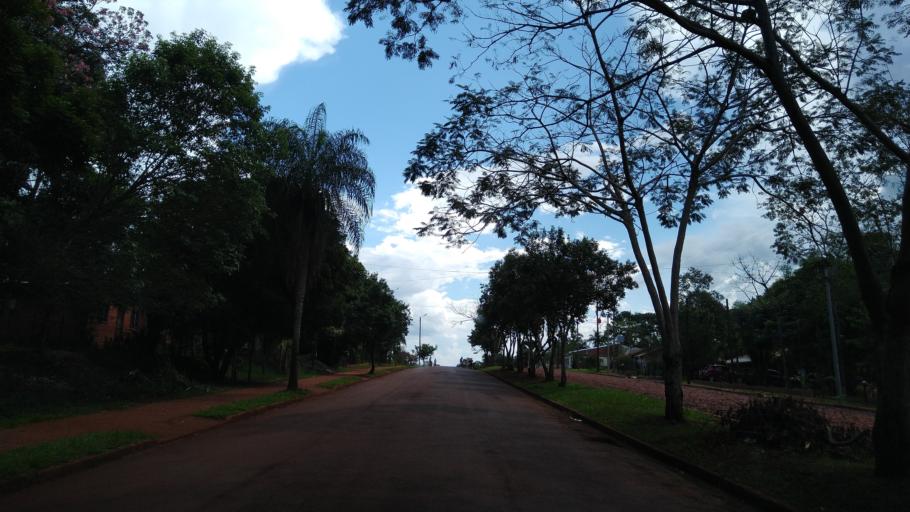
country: AR
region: Misiones
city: Puerto Libertad
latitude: -25.9669
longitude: -54.5913
